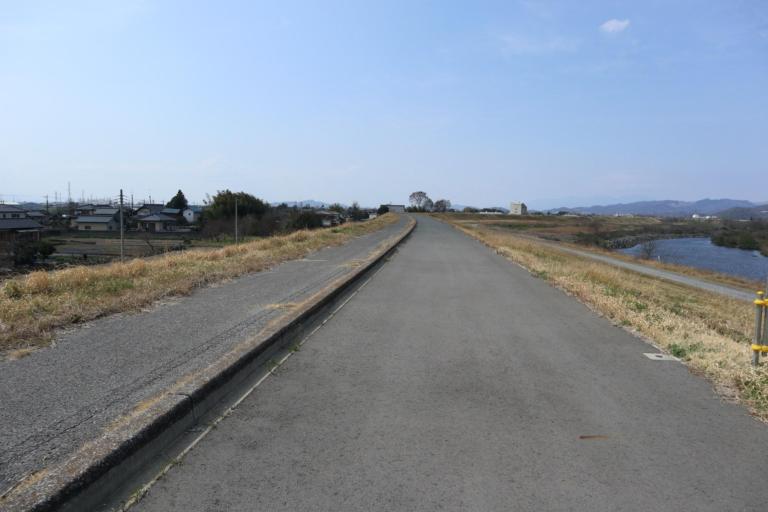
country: JP
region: Gunma
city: Tatebayashi
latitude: 36.2939
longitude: 139.5136
